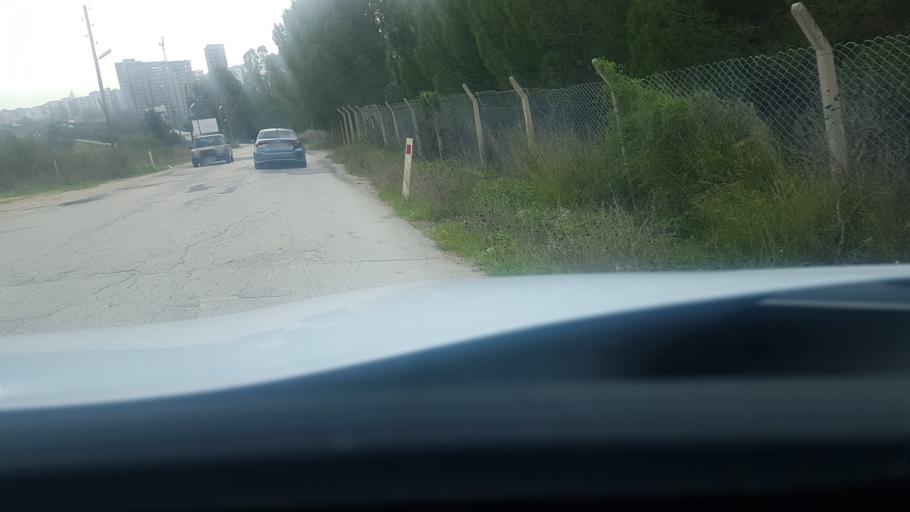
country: TR
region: Adana
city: Seyhan
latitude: 37.0579
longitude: 35.2549
